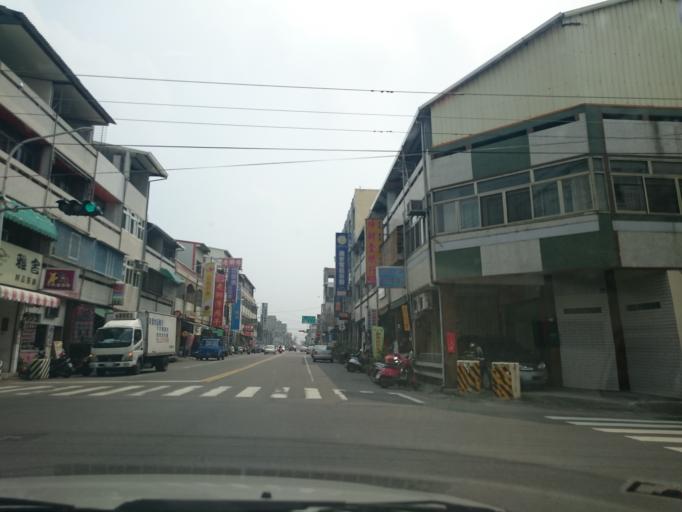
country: TW
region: Taiwan
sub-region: Nantou
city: Nantou
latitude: 23.8744
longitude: 120.5283
